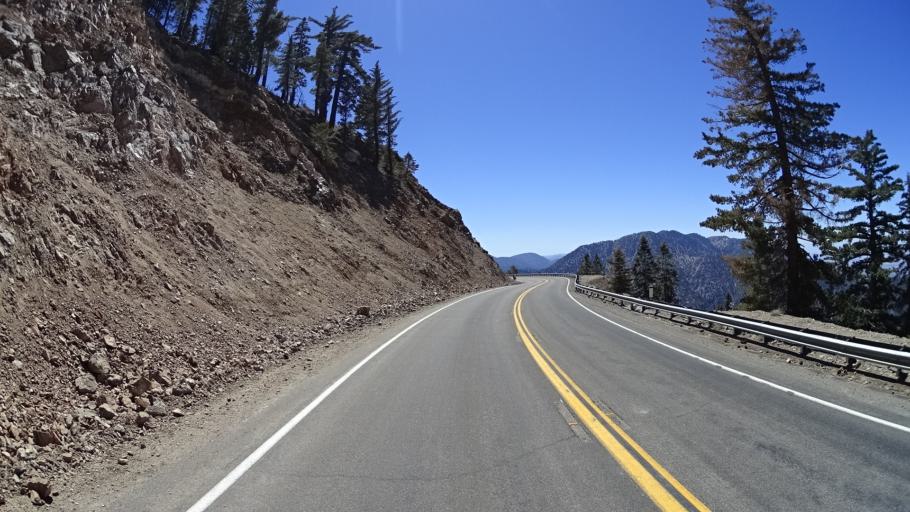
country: US
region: California
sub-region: San Bernardino County
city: Wrightwood
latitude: 34.3602
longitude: -117.8108
